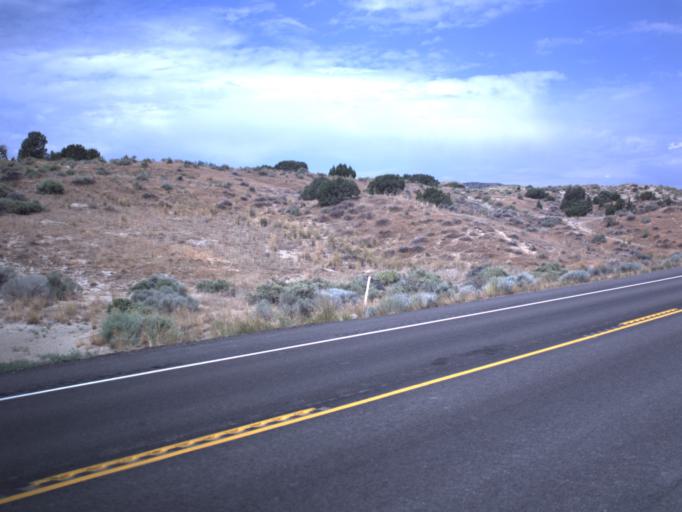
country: US
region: Utah
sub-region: Uintah County
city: Naples
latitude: 40.3464
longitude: -109.4872
